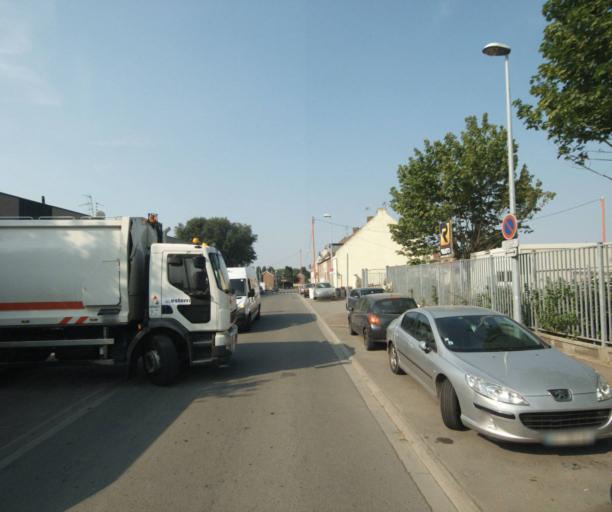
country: FR
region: Nord-Pas-de-Calais
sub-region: Departement du Nord
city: Neuville-en-Ferrain
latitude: 50.7390
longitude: 3.1430
